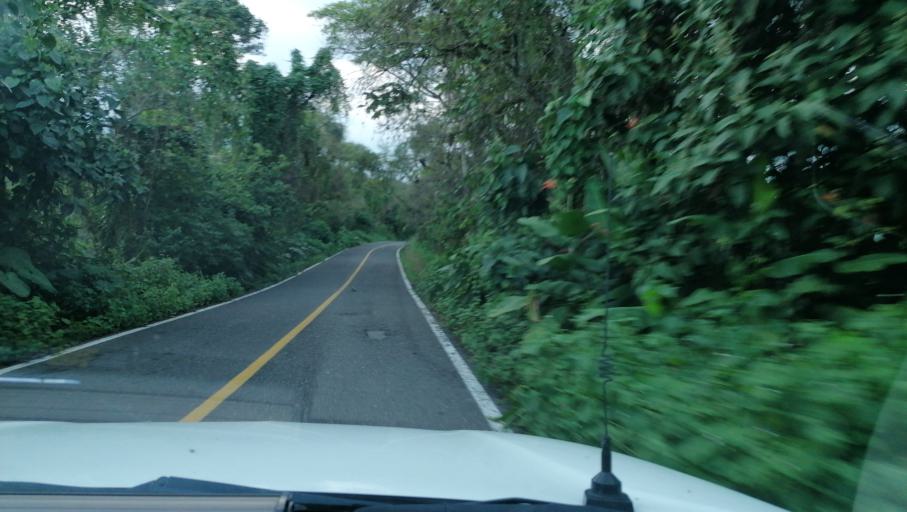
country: MX
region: Chiapas
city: Pichucalco
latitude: 17.5148
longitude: -93.1549
